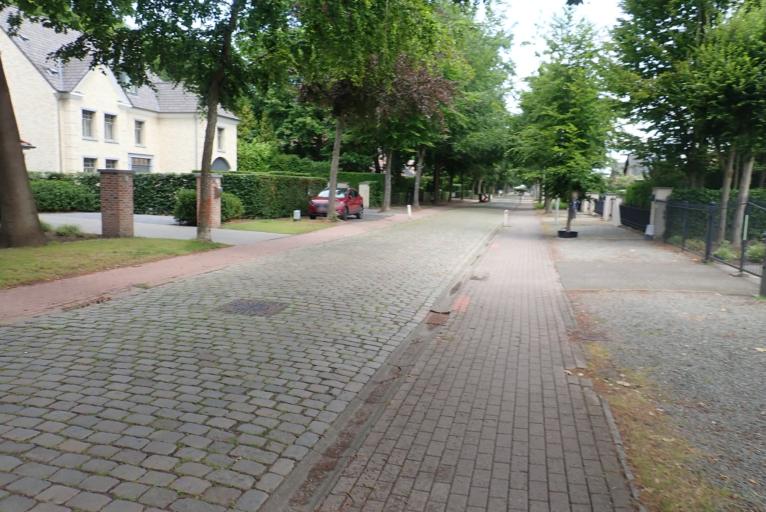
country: BE
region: Flanders
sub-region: Provincie Antwerpen
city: Essen
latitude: 51.4511
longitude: 4.4432
